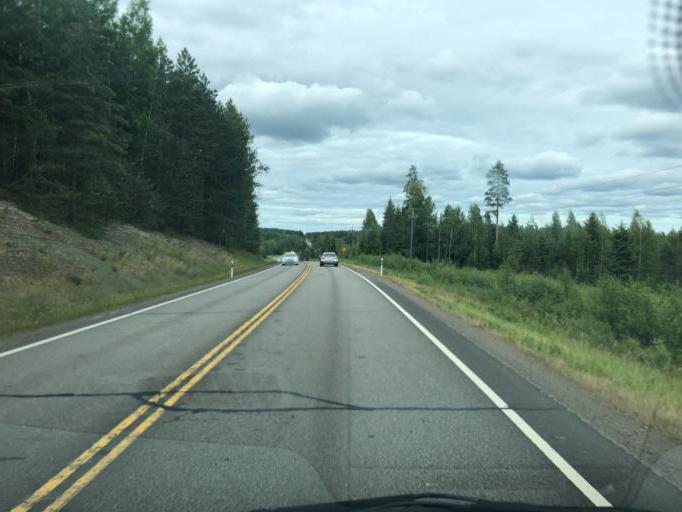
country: FI
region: Kymenlaakso
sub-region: Kouvola
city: Kouvola
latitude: 60.9744
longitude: 26.9030
